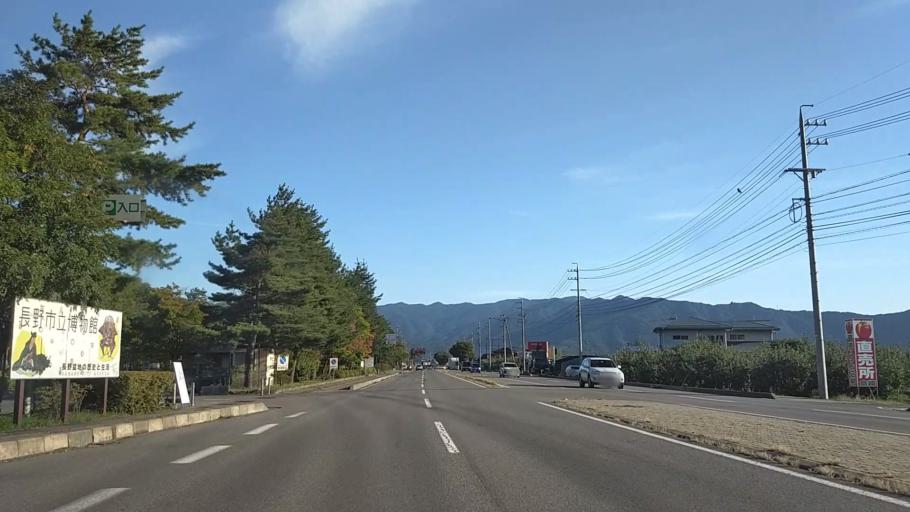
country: JP
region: Nagano
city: Nagano-shi
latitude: 36.5905
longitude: 138.1863
